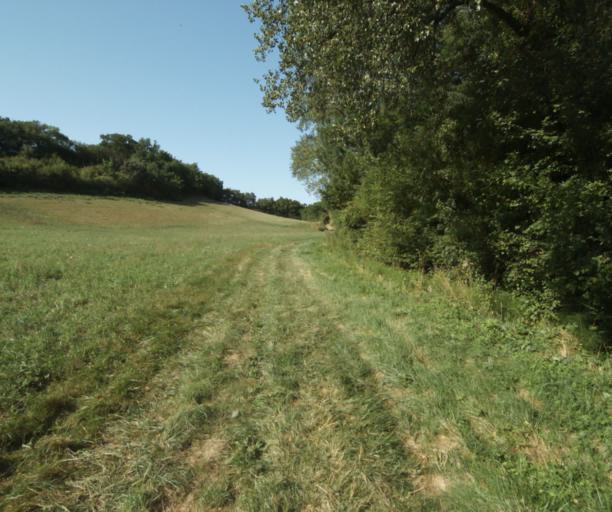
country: FR
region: Midi-Pyrenees
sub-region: Departement de la Haute-Garonne
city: Avignonet-Lauragais
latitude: 43.4204
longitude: 1.8248
